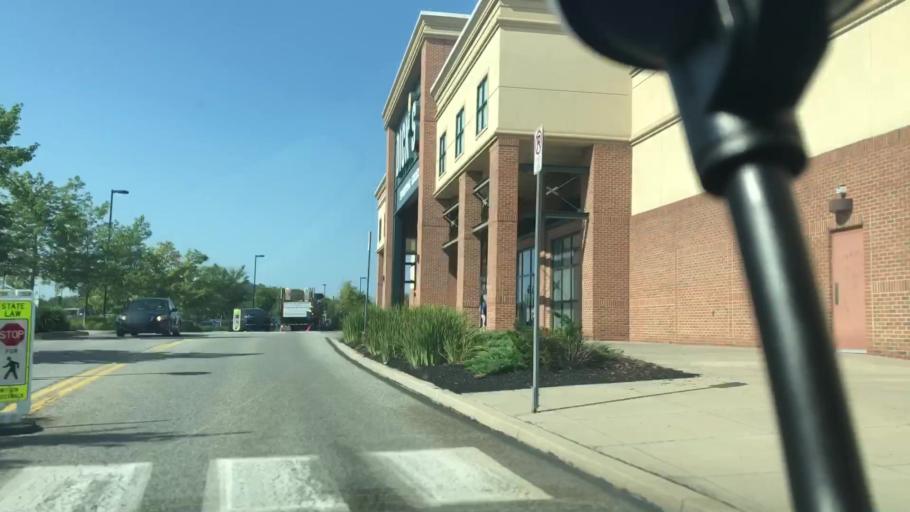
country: US
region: Pennsylvania
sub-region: Montgomery County
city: Collegeville
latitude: 40.1643
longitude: -75.4785
